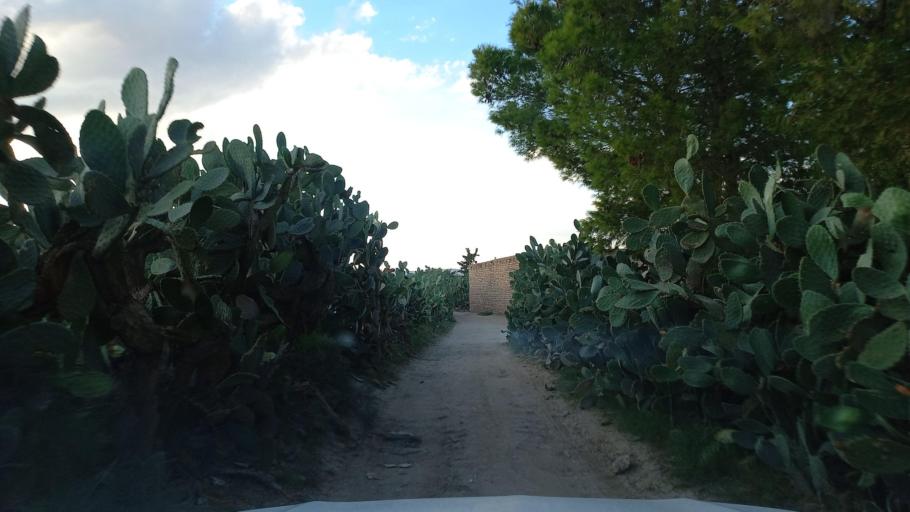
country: TN
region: Al Qasrayn
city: Sbiba
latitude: 35.3784
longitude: 9.0545
